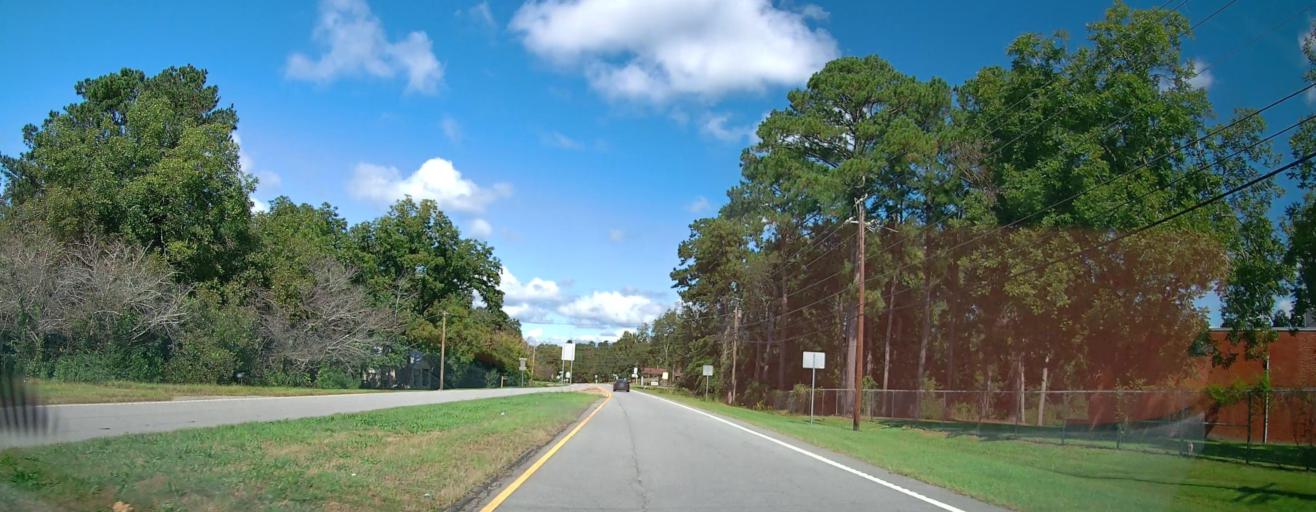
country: US
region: Georgia
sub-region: Bibb County
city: Macon
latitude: 32.8138
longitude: -83.5688
